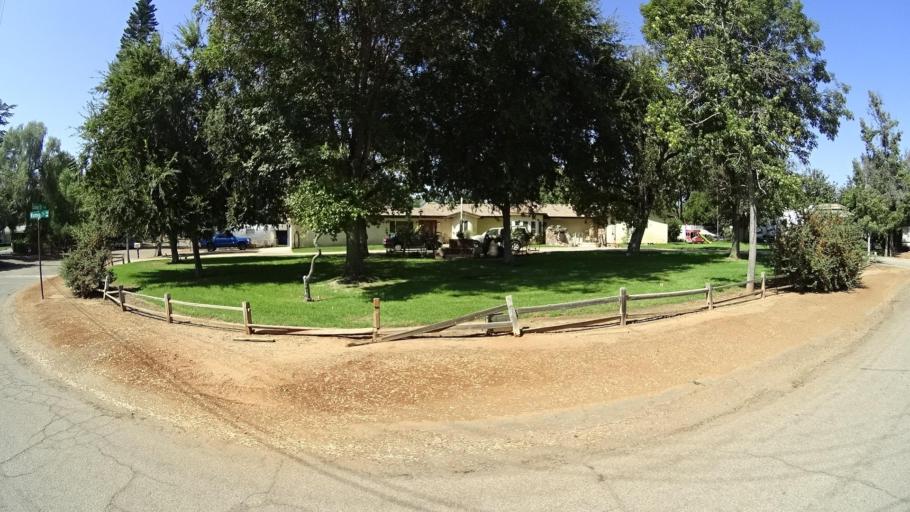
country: US
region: California
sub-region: San Diego County
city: Granite Hills
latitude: 32.8016
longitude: -116.9150
